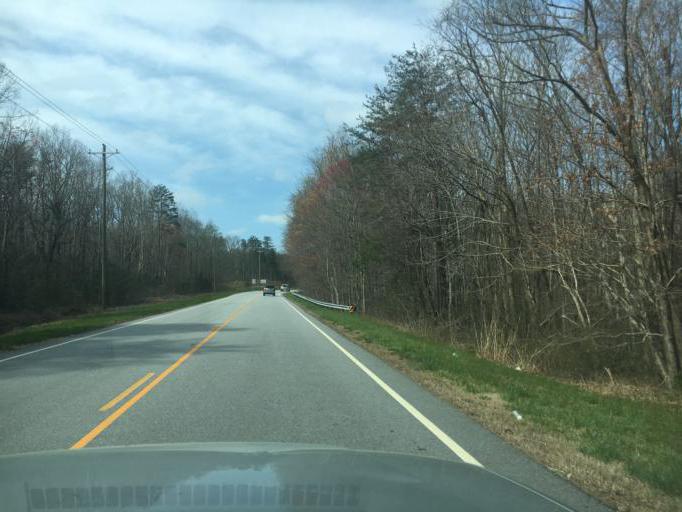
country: US
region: South Carolina
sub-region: Greenville County
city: Tigerville
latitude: 35.1239
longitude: -82.3079
